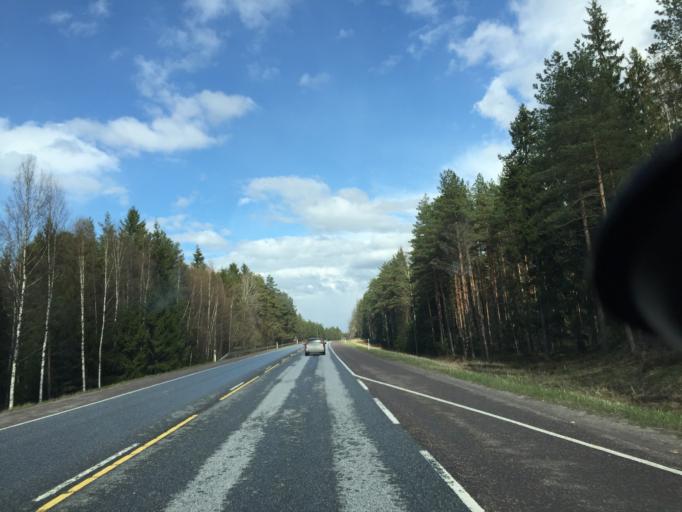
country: FI
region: Uusimaa
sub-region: Raaseporin
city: Karis
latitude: 60.0814
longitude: 23.7273
